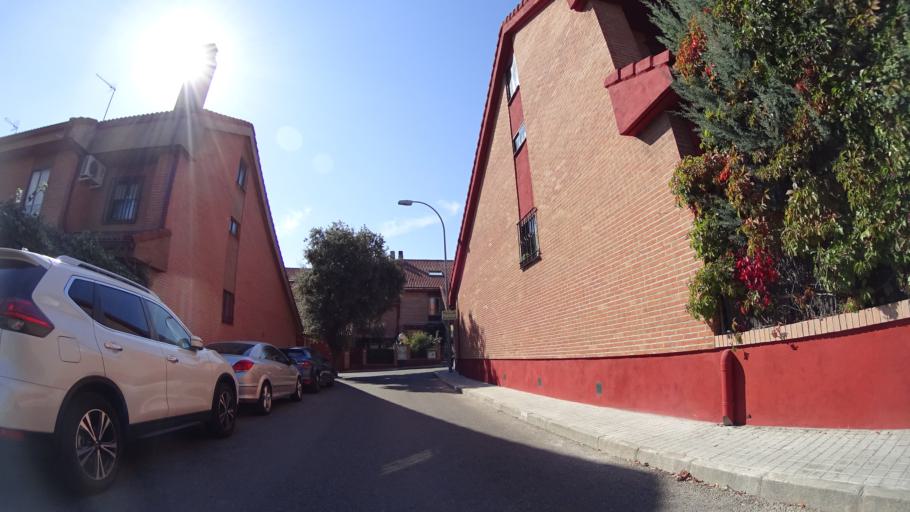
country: ES
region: Madrid
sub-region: Provincia de Madrid
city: Collado-Villalba
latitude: 40.6179
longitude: -4.0056
